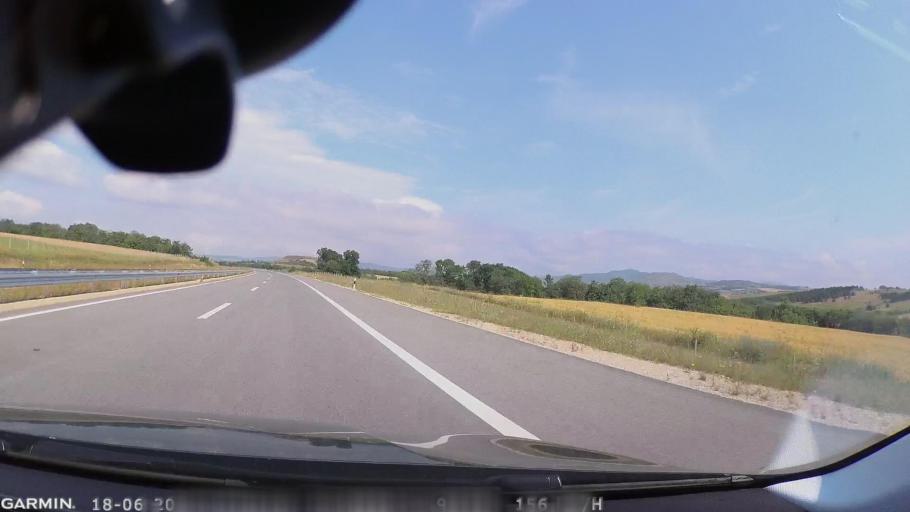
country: MK
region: Sveti Nikole
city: Gorobinci
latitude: 41.9105
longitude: 21.9010
